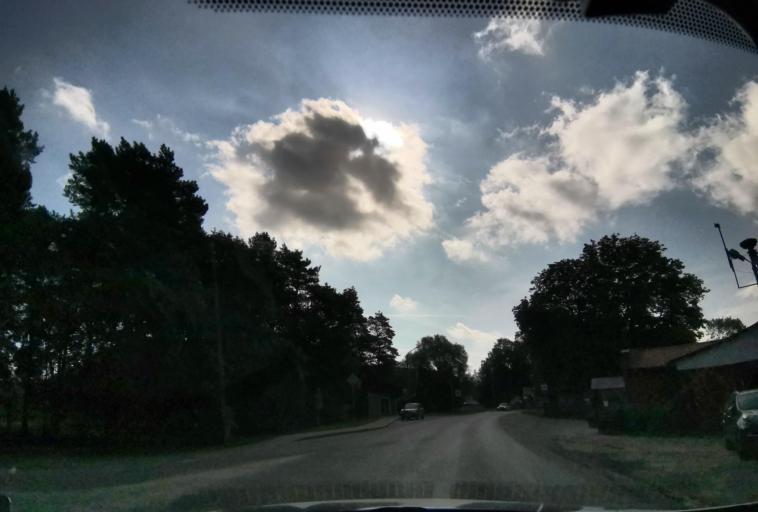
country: RU
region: Kaliningrad
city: Chernyakhovsk
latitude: 54.6505
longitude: 21.8141
